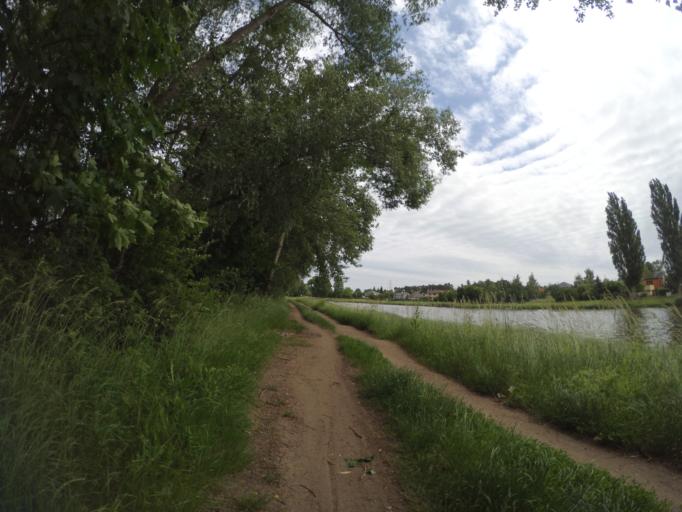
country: CZ
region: Central Bohemia
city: Celakovice
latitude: 50.1727
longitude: 14.7722
